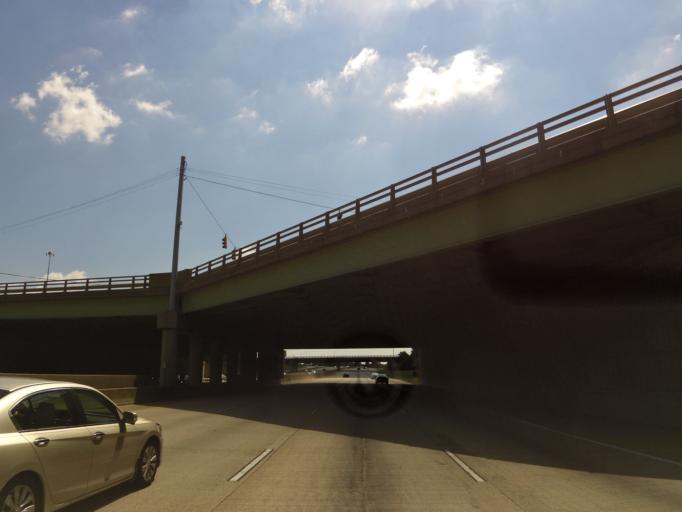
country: US
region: North Carolina
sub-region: Mecklenburg County
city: Charlotte
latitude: 35.2485
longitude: -80.8961
